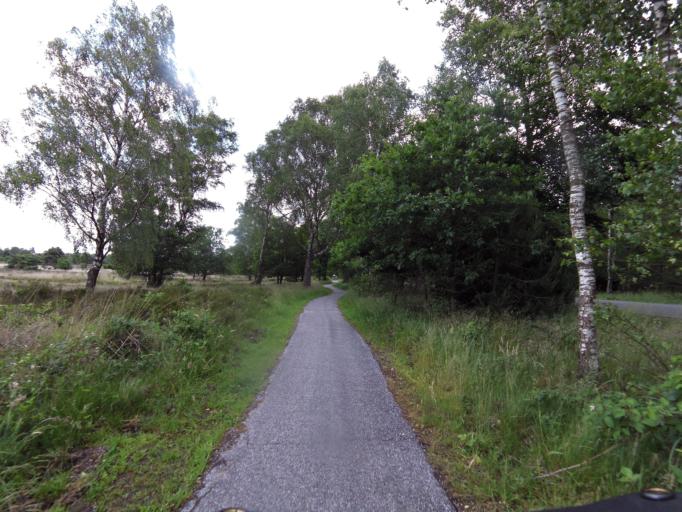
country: NL
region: Gelderland
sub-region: Gemeente Nunspeet
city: Nunspeet
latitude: 52.3277
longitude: 5.7699
